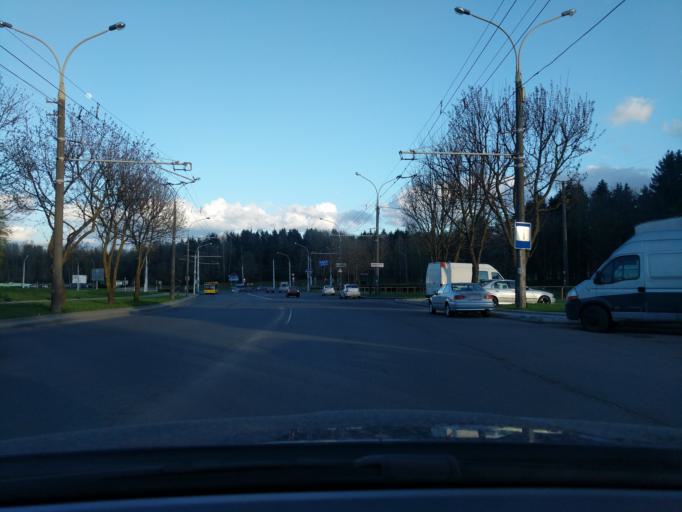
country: BY
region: Minsk
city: Novoye Medvezhino
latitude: 53.8915
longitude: 27.4536
